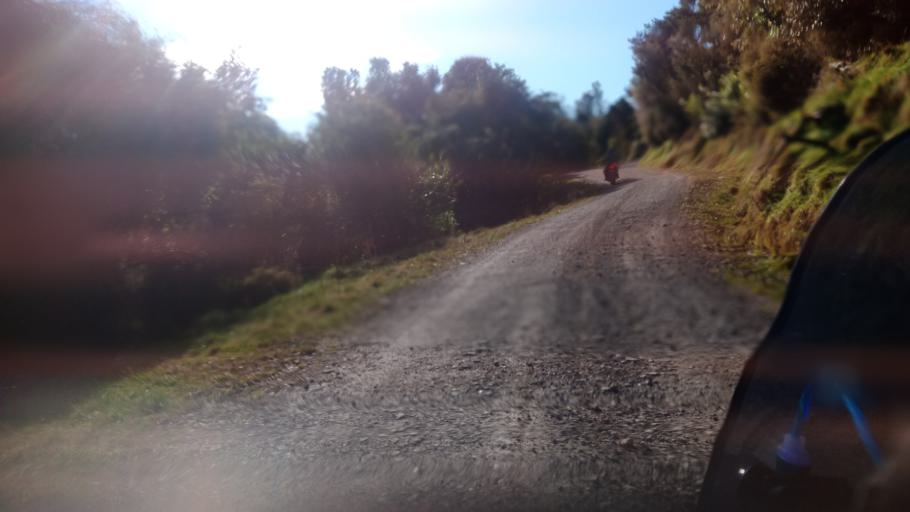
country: NZ
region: Hawke's Bay
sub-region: Wairoa District
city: Wairoa
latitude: -38.6659
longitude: 177.5160
